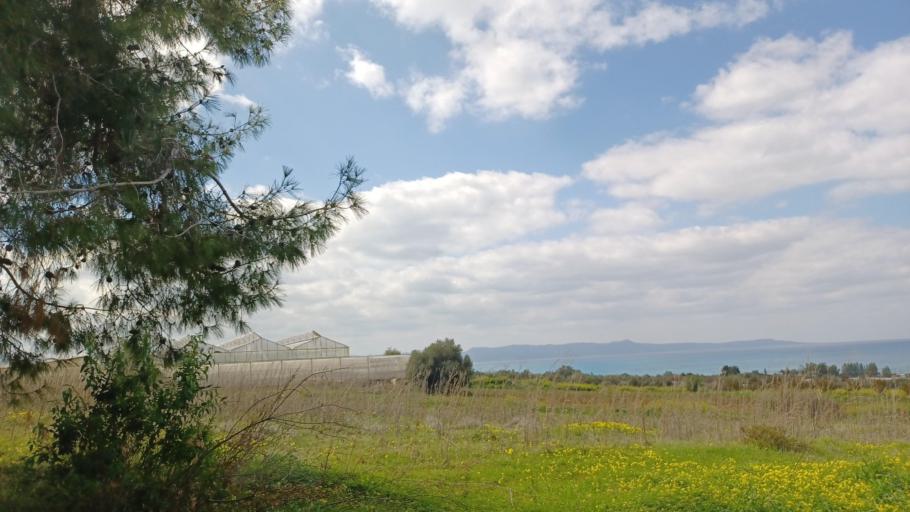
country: CY
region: Pafos
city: Polis
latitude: 35.1053
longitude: 32.5140
